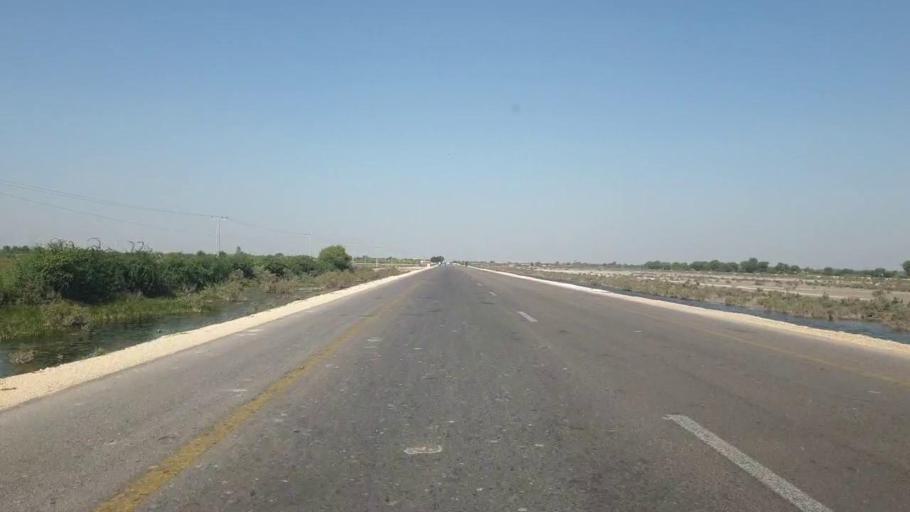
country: PK
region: Sindh
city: Talhar
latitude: 24.8418
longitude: 68.8163
